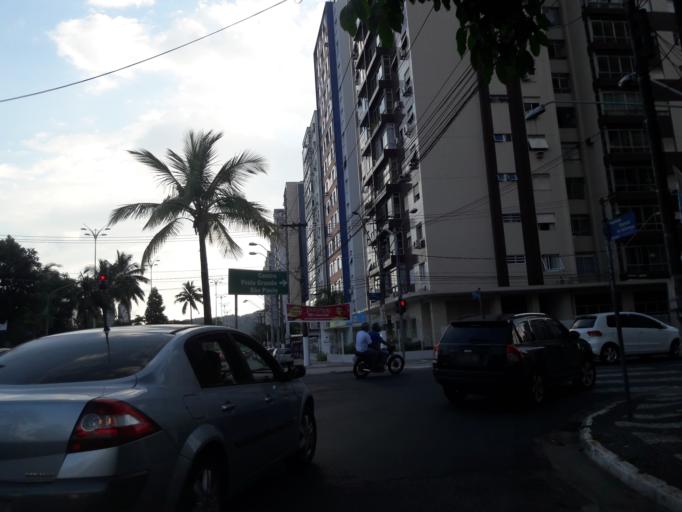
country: BR
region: Sao Paulo
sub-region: Sao Vicente
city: Sao Vicente
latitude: -23.9717
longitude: -46.3695
